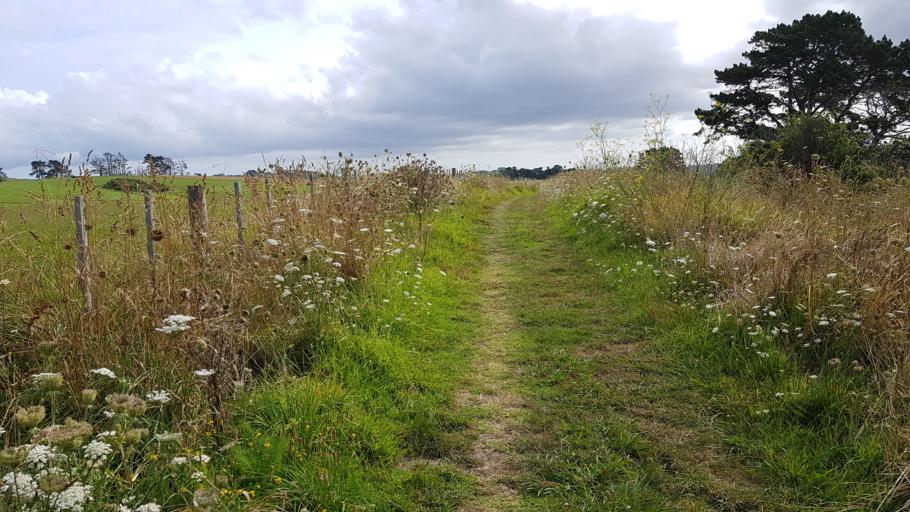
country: NZ
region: Auckland
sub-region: Auckland
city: Rothesay Bay
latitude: -36.6621
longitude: 174.7422
